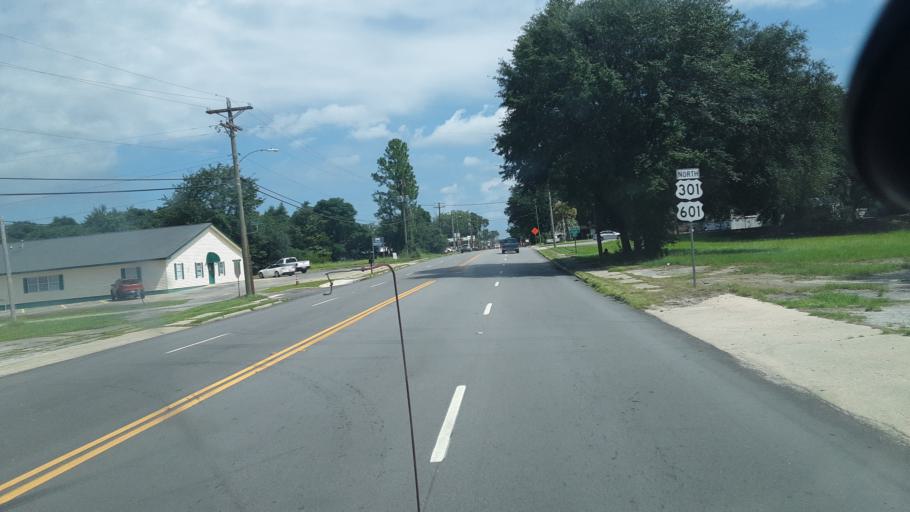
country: US
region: South Carolina
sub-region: Bamberg County
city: Bamberg
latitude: 33.2855
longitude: -81.0393
